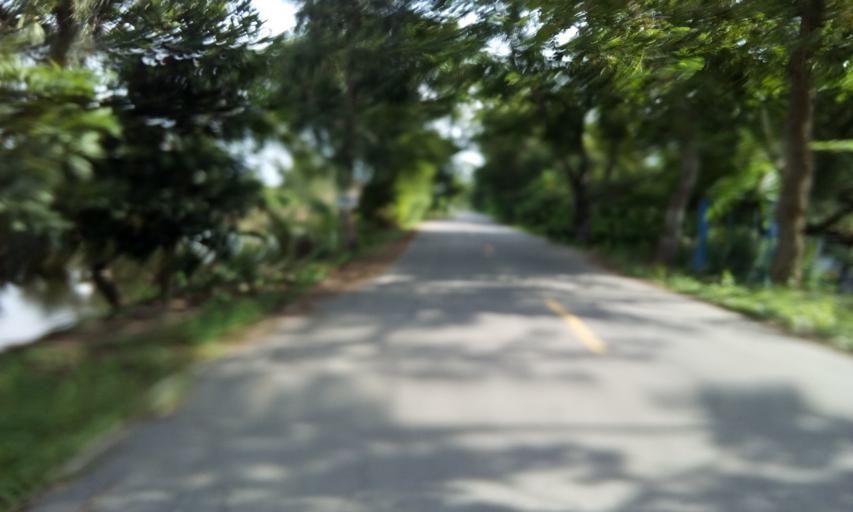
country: TH
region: Pathum Thani
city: Nong Suea
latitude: 14.1893
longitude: 100.8230
